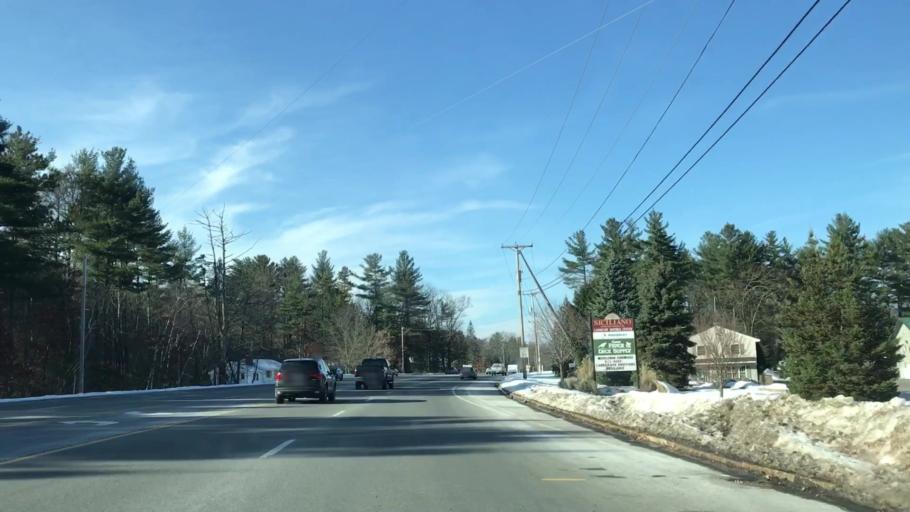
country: US
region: New Hampshire
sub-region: Hillsborough County
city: Milford
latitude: 42.8158
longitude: -71.5994
